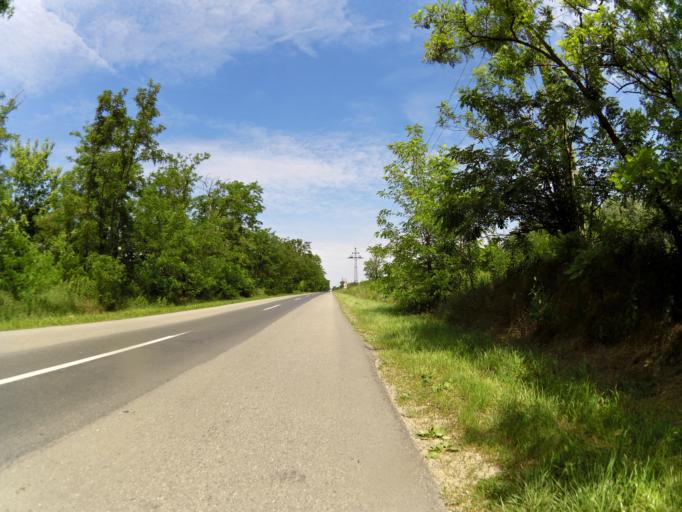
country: HU
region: Csongrad
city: Sandorfalva
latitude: 46.3819
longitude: 20.1151
